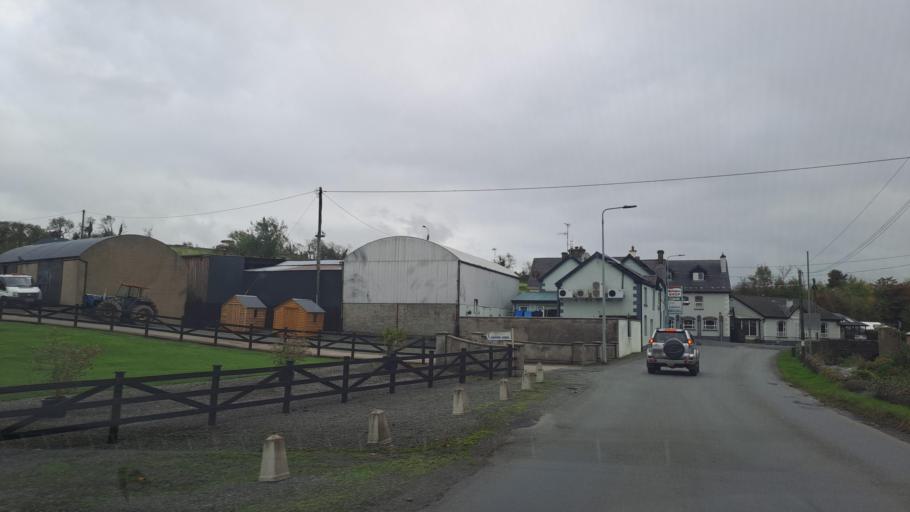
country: IE
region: Ulster
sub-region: An Cabhan
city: Cootehill
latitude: 53.9809
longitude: -7.0476
